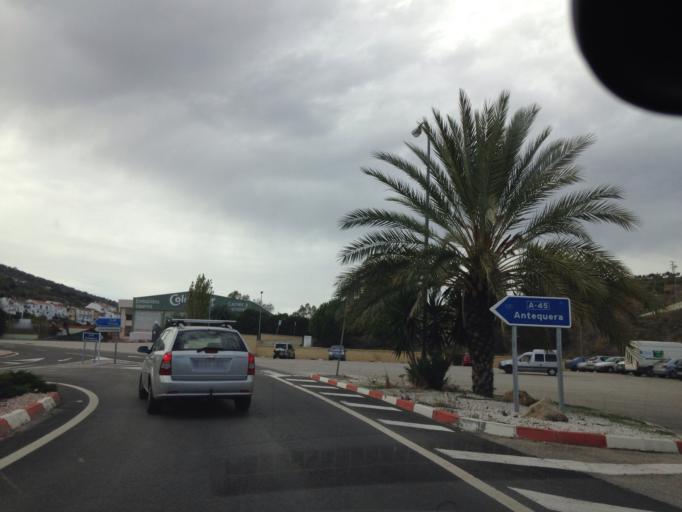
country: ES
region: Andalusia
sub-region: Provincia de Malaga
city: Casabermeja
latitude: 36.8980
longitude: -4.4295
